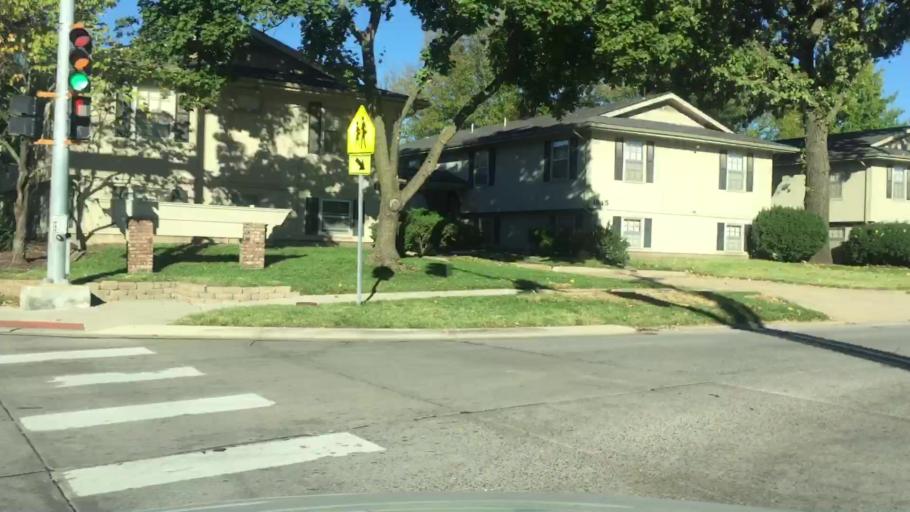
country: US
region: Kansas
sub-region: Douglas County
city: Lawrence
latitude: 38.9501
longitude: -95.2382
